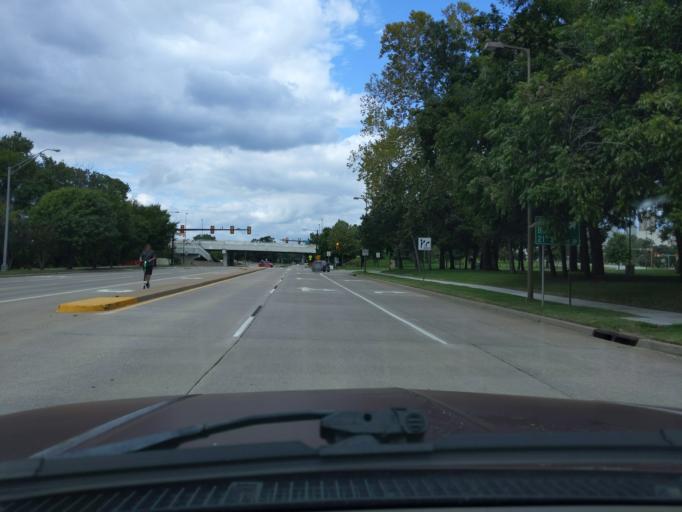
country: US
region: Oklahoma
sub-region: Tulsa County
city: Tulsa
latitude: 36.1314
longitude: -95.9891
